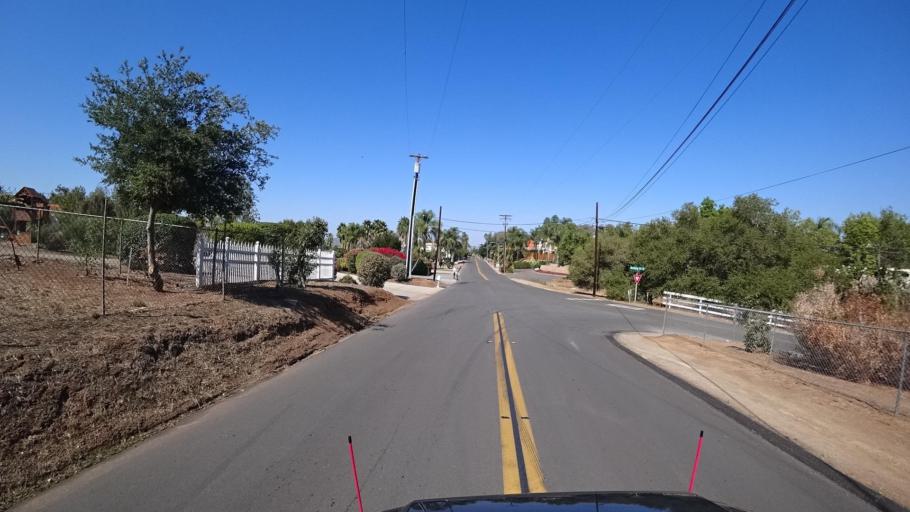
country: US
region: California
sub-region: San Diego County
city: Granite Hills
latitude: 32.7935
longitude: -116.9025
